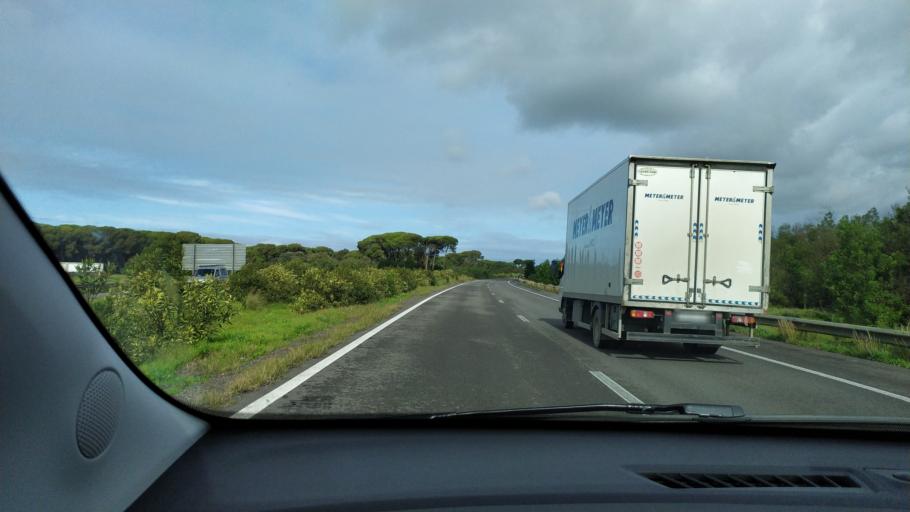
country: MA
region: Tanger-Tetouan
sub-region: Larache
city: Larache
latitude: 35.1294
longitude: -6.1462
